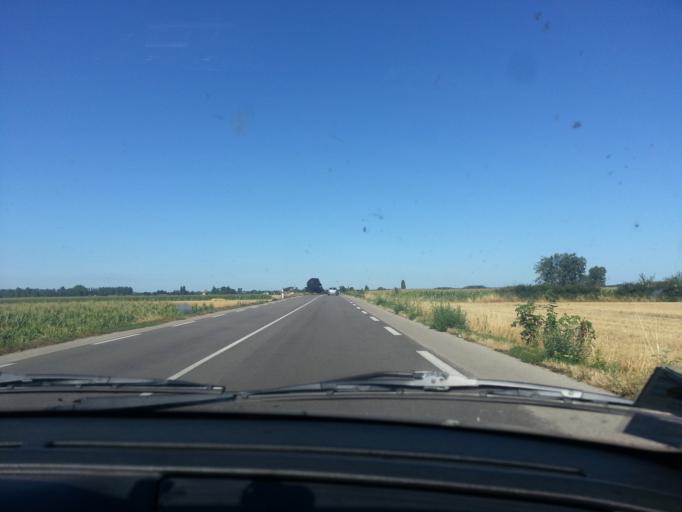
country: FR
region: Bourgogne
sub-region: Departement de Saone-et-Loire
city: Sassenay
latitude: 46.8105
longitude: 4.9523
